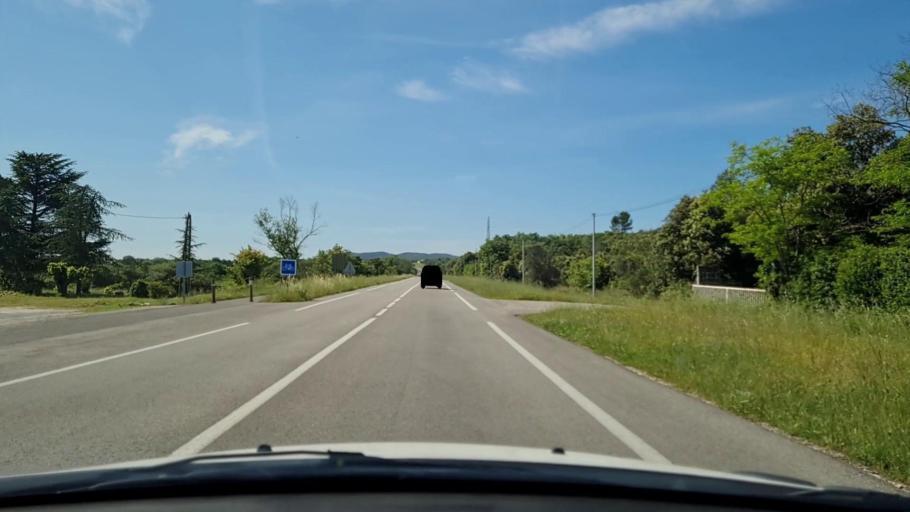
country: FR
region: Languedoc-Roussillon
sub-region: Departement du Gard
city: Vezenobres
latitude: 44.0416
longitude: 4.1466
